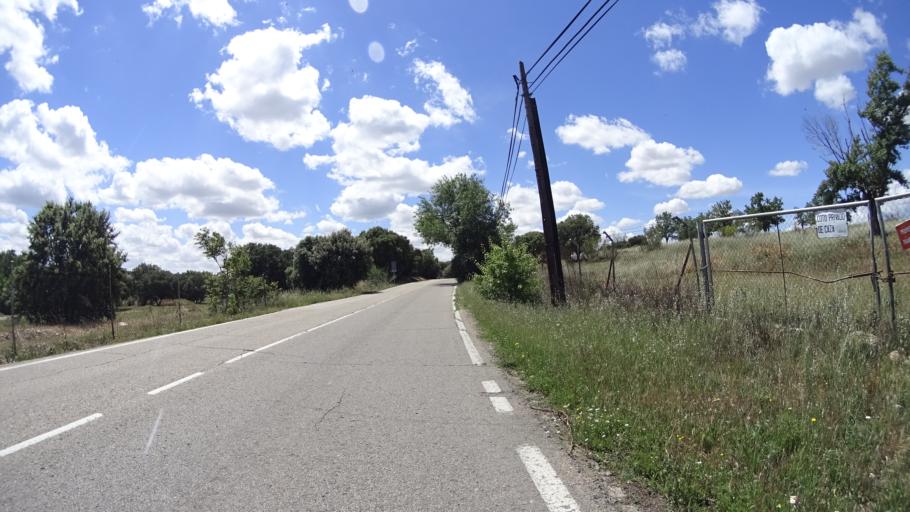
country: ES
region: Madrid
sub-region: Provincia de Madrid
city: Villanueva del Pardillo
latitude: 40.4617
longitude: -3.9456
